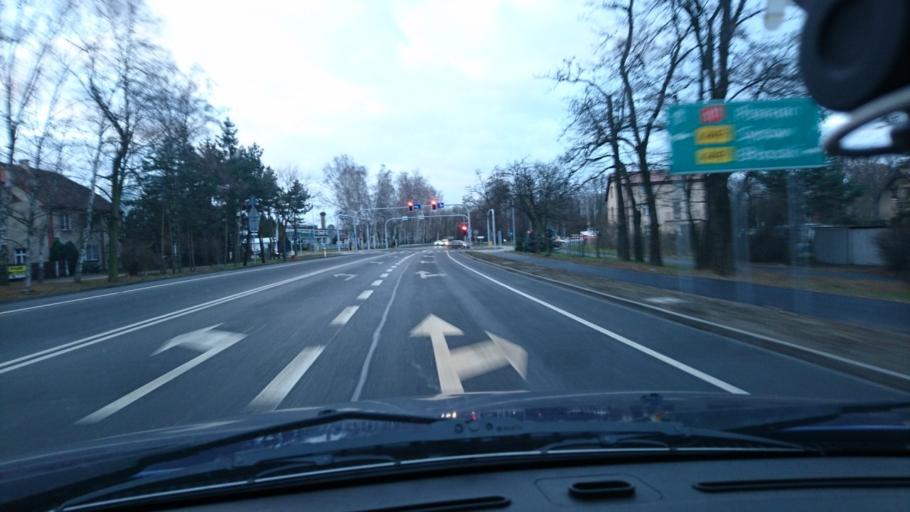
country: PL
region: Greater Poland Voivodeship
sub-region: Powiat ostrzeszowski
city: Ostrzeszow
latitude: 51.4207
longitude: 17.9269
